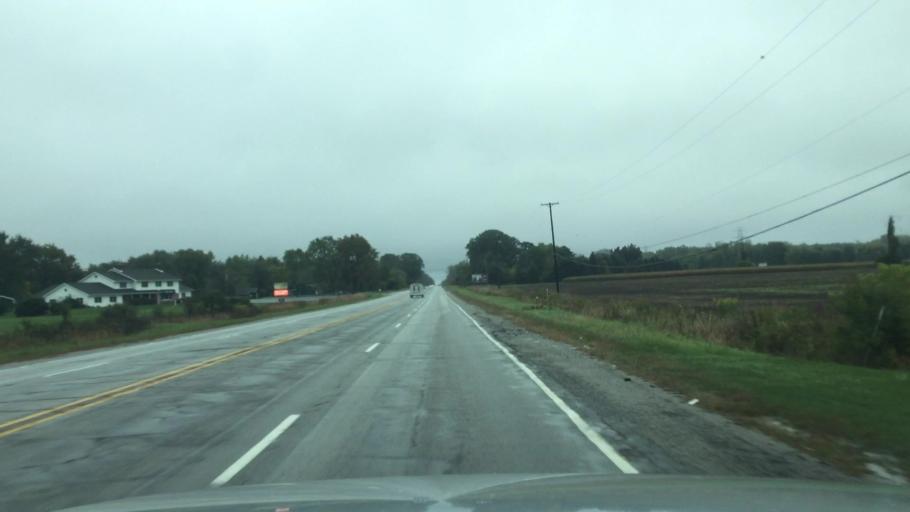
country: US
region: Michigan
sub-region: Saginaw County
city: Bridgeport
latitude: 43.3283
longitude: -83.8285
